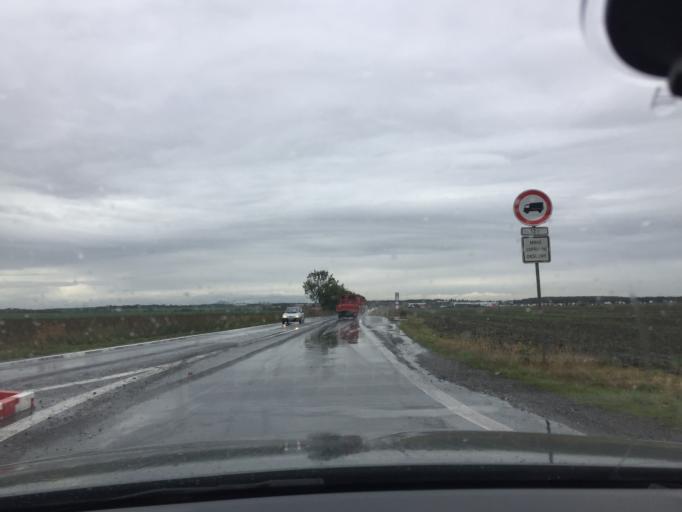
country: CZ
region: Central Bohemia
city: Zdiby
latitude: 50.1829
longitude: 14.4402
